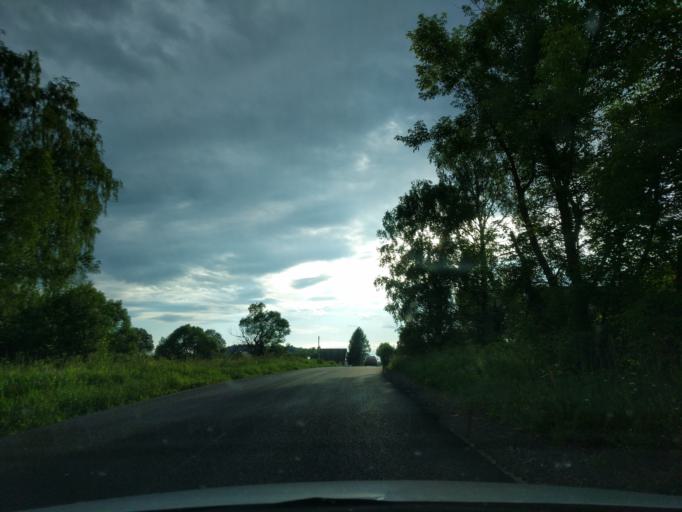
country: RU
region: Kaluga
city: Myatlevo
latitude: 54.8008
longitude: 35.7242
